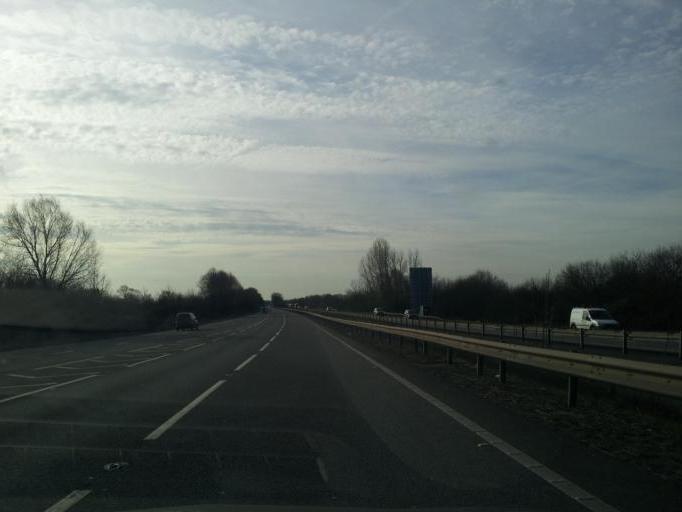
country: GB
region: England
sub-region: Cambridgeshire
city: Brampton
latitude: 52.3280
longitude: -0.2474
